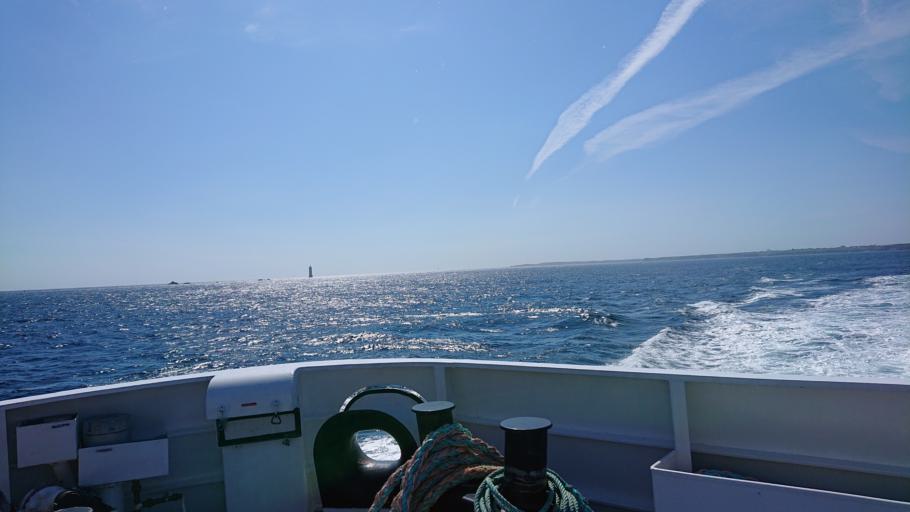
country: FR
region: Brittany
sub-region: Departement du Finistere
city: Porspoder
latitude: 48.4465
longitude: -4.9987
